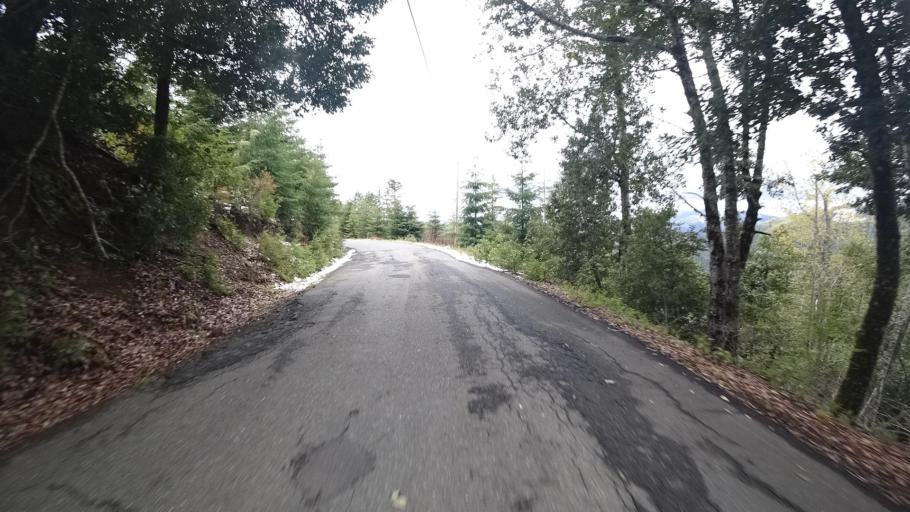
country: US
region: California
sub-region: Humboldt County
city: Blue Lake
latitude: 40.8826
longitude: -123.8747
